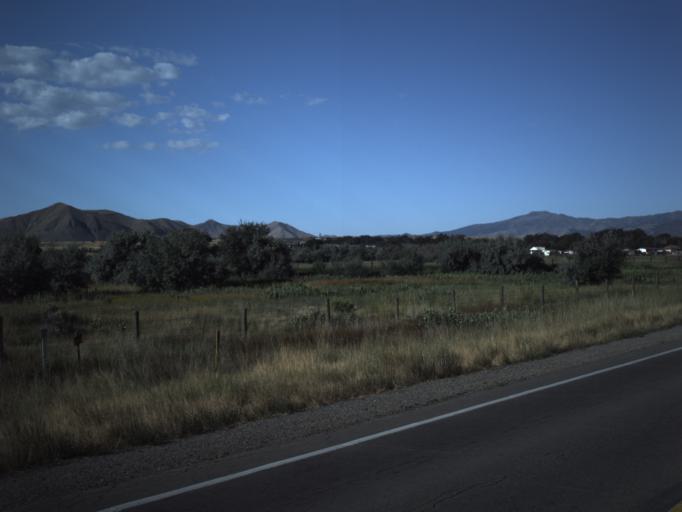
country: US
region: Utah
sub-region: Utah County
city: Genola
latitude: 39.9540
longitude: -111.8907
